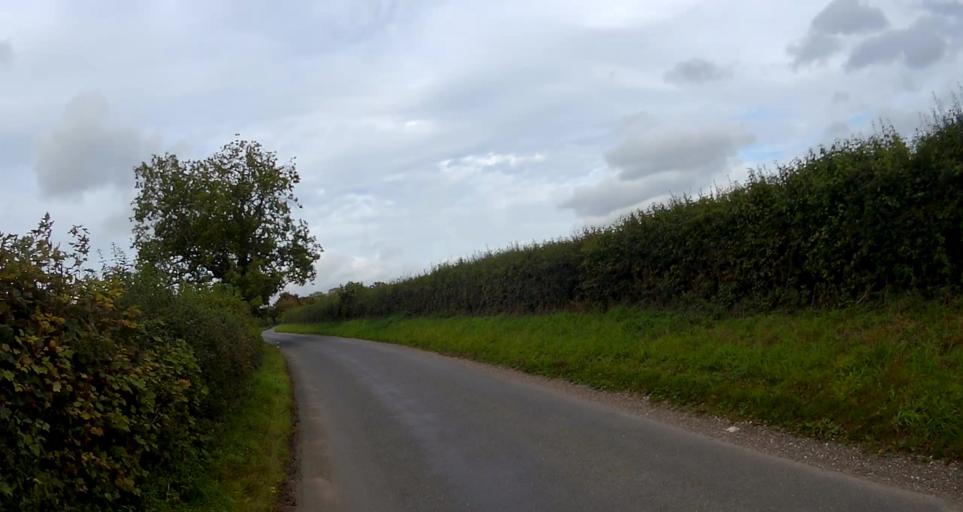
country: GB
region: England
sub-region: Hampshire
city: Four Marks
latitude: 51.1002
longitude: -1.1420
